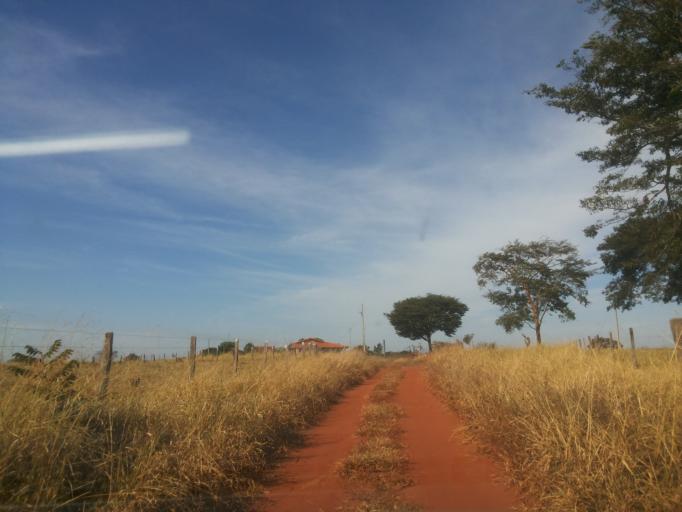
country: BR
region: Minas Gerais
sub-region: Ituiutaba
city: Ituiutaba
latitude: -19.1258
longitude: -49.3805
